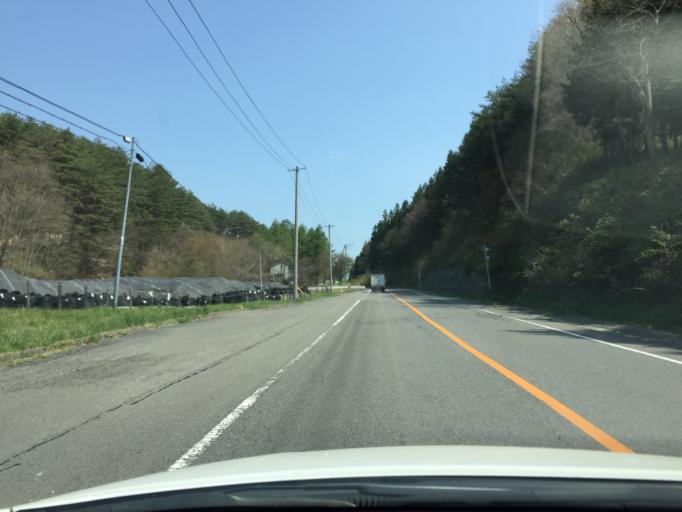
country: JP
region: Fukushima
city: Funehikimachi-funehiki
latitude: 37.4460
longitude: 140.7813
